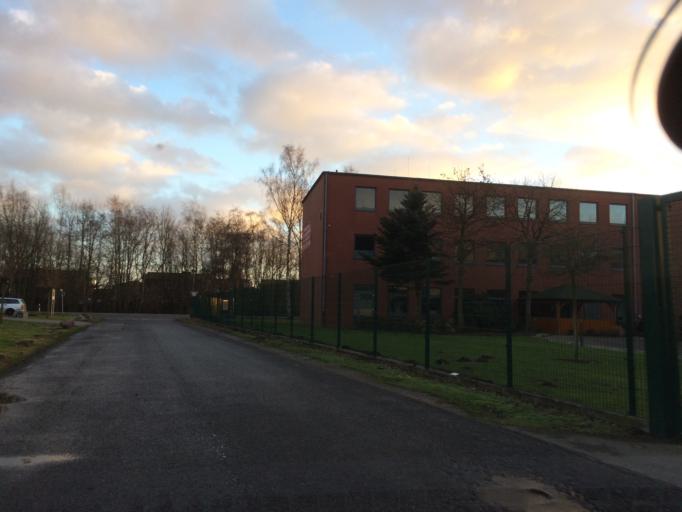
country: DE
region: North Rhine-Westphalia
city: Dorsten
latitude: 51.6746
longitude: 6.9969
